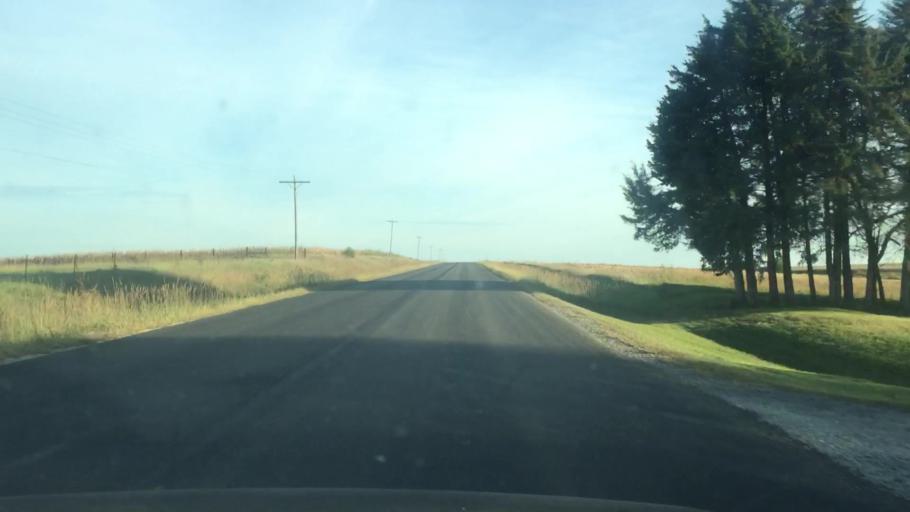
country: US
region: Kansas
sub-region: Marshall County
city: Marysville
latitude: 39.9015
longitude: -96.6010
